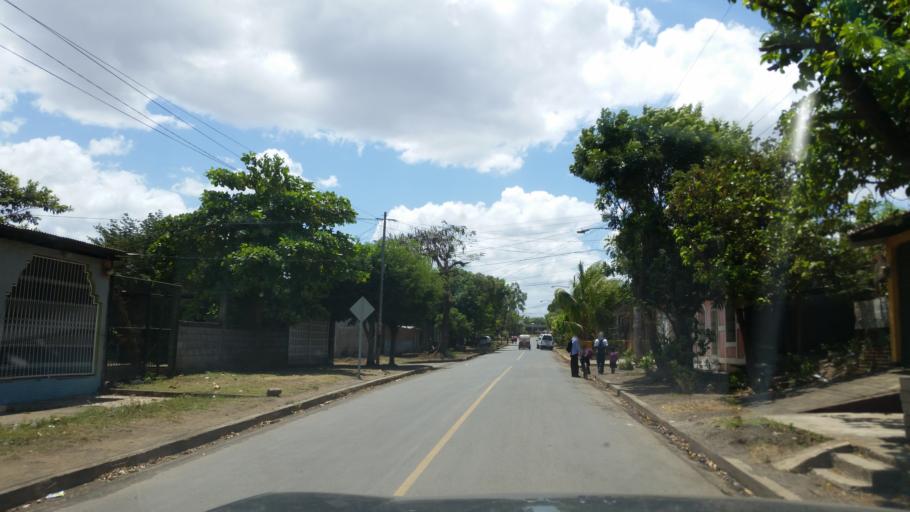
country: NI
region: Managua
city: Managua
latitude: 12.1149
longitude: -86.2076
